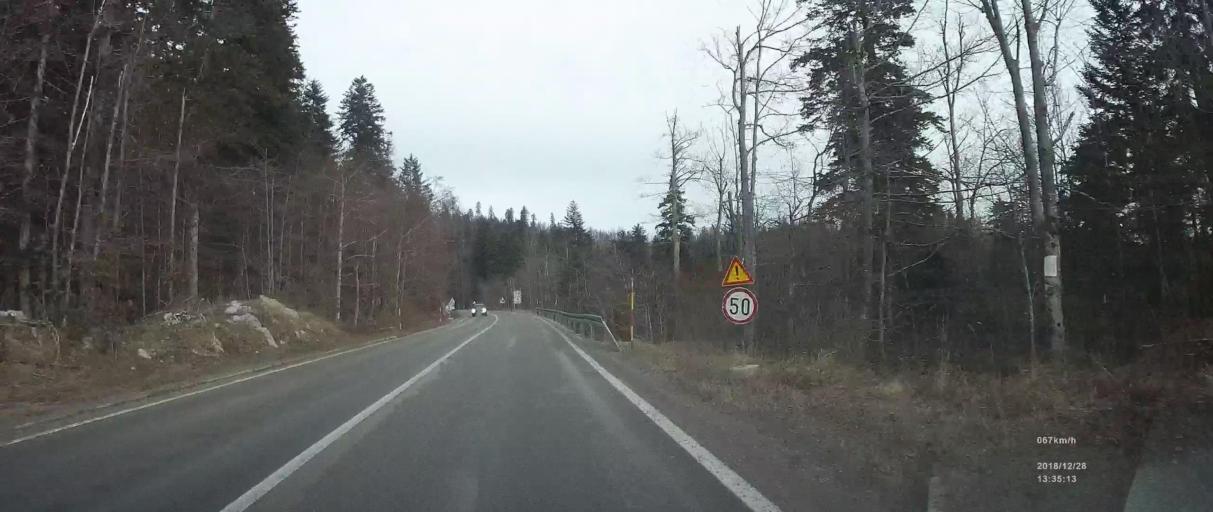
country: HR
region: Primorsko-Goranska
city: Hreljin
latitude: 45.3476
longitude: 14.6904
